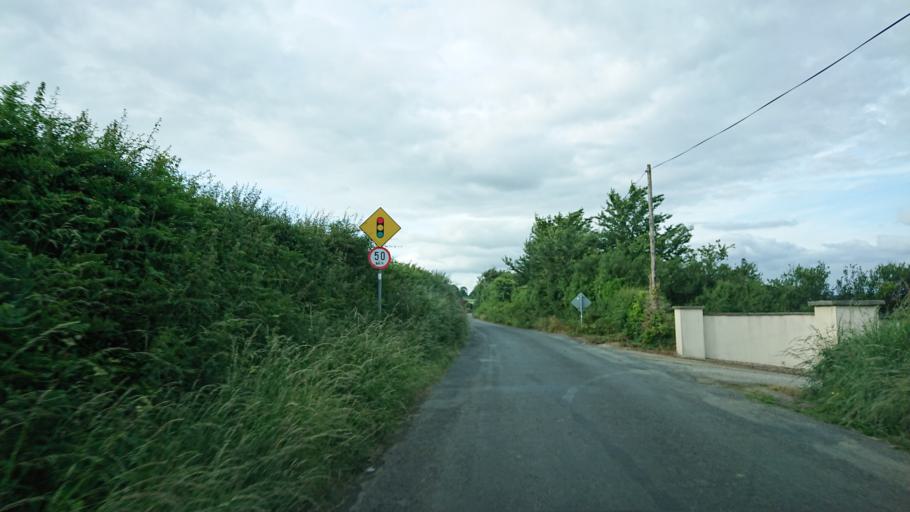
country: IE
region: Munster
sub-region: Waterford
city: Tra Mhor
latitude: 52.2216
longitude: -7.1819
